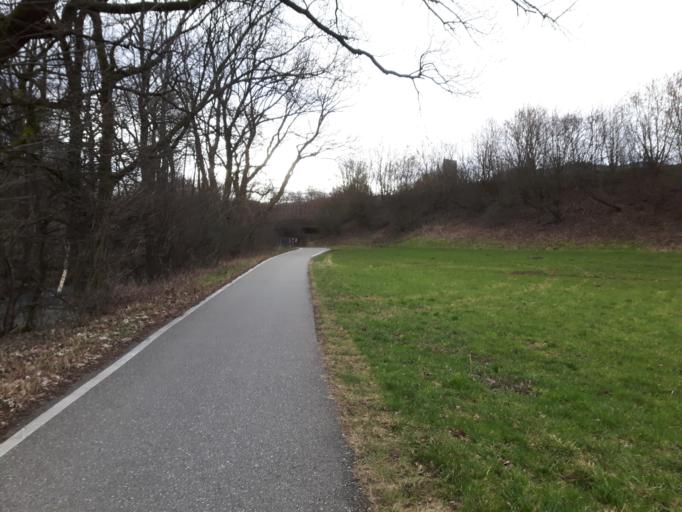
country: DE
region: Baden-Wuerttemberg
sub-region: Freiburg Region
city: Kirchzarten
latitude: 47.9793
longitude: 7.9140
